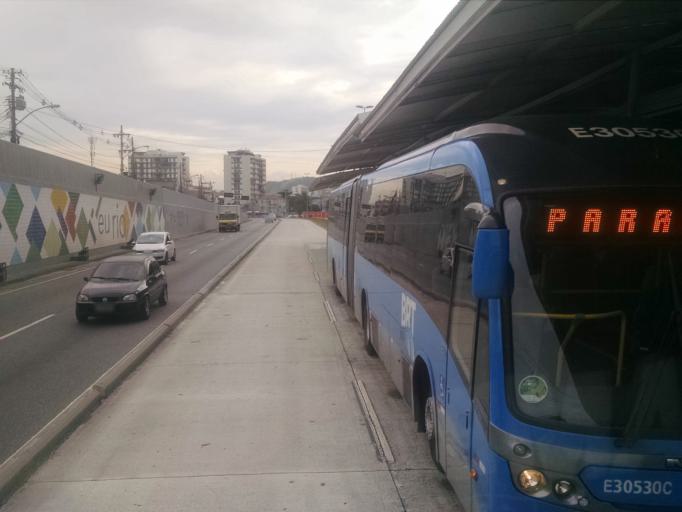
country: BR
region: Rio de Janeiro
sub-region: Sao Joao De Meriti
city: Sao Joao de Meriti
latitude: -22.8824
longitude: -43.3420
